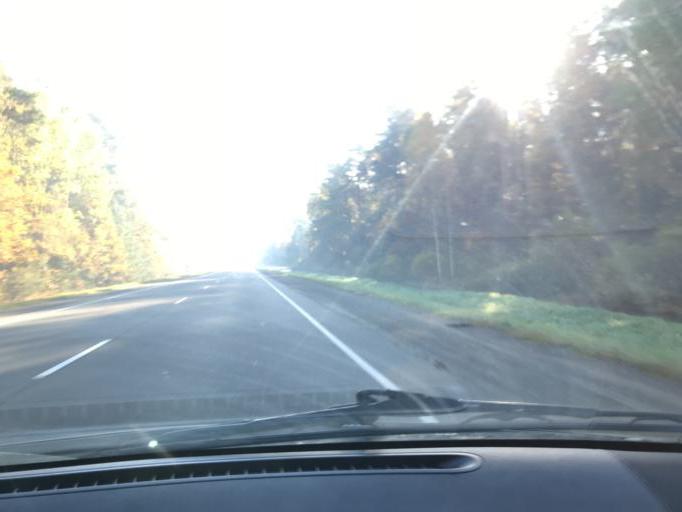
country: BY
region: Brest
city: Horad Luninyets
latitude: 52.2903
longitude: 26.7757
